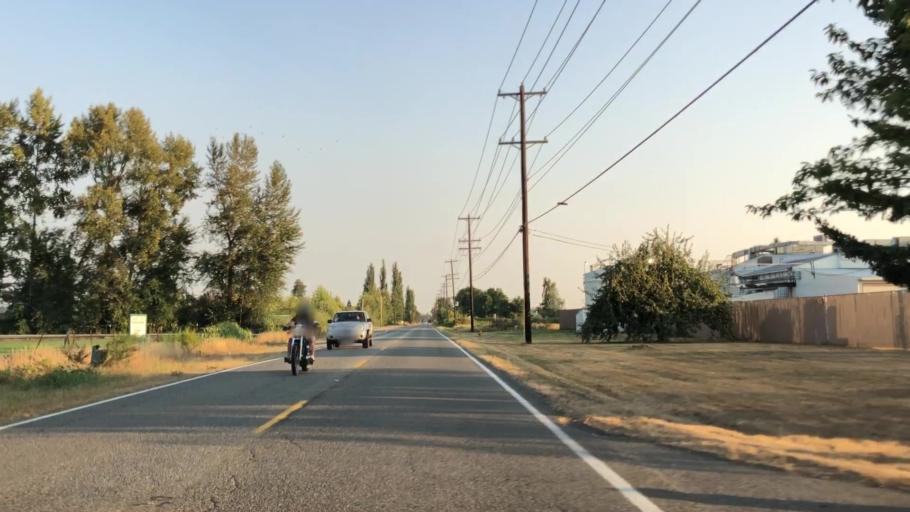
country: US
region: Washington
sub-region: Snohomish County
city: Smokey Point
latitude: 48.1495
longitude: -122.1616
